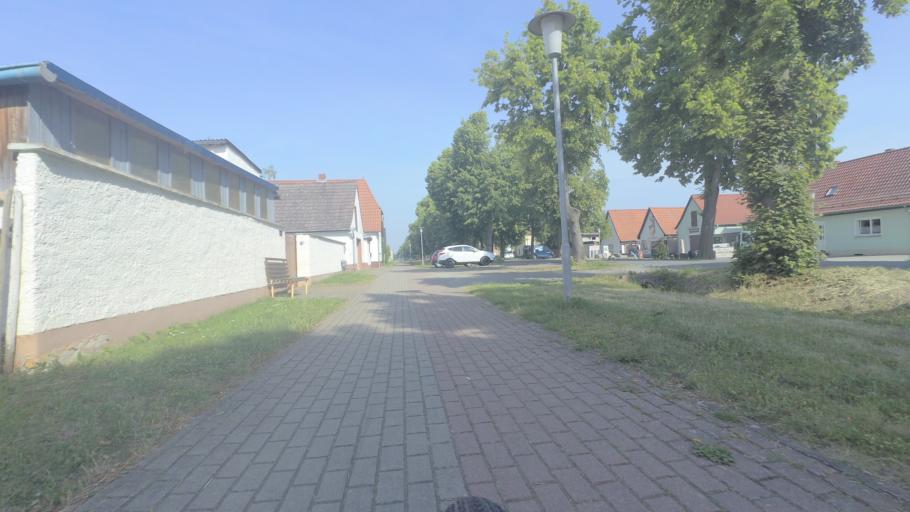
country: DE
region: Saxony-Anhalt
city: Nachterstedt
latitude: 51.7641
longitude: 11.3512
